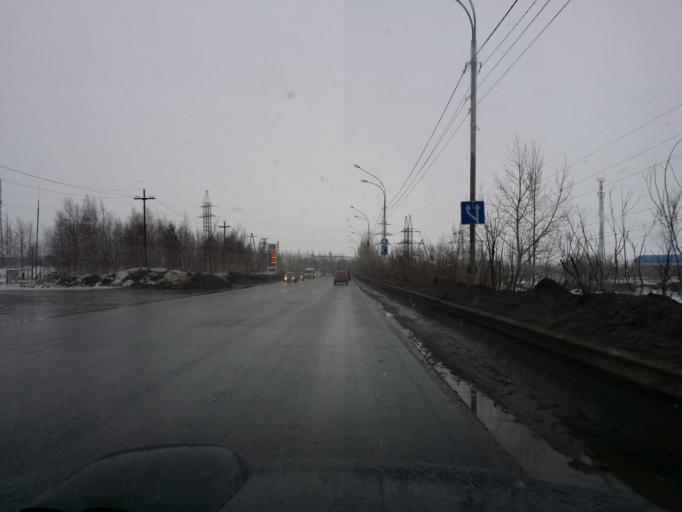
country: RU
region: Khanty-Mansiyskiy Avtonomnyy Okrug
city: Nizhnevartovsk
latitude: 60.9293
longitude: 76.5313
